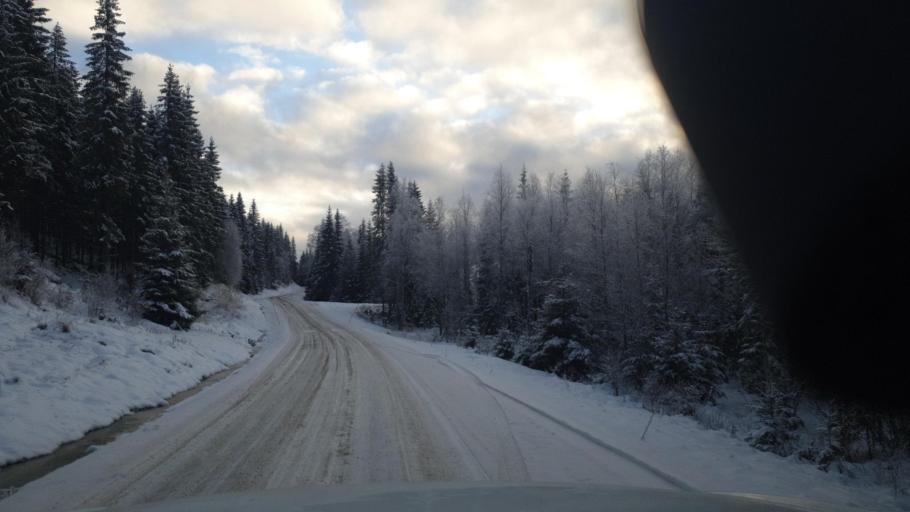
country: SE
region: Vaermland
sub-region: Eda Kommun
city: Charlottenberg
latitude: 60.0975
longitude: 12.6103
